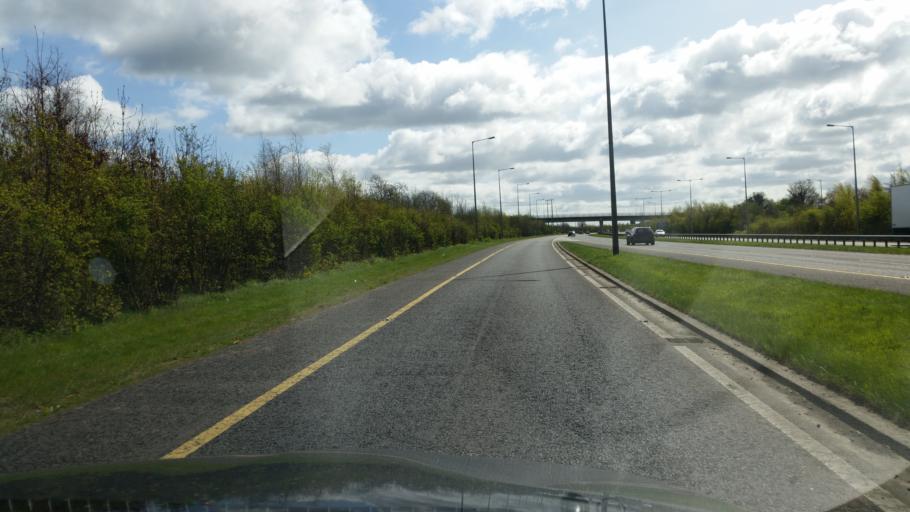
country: IE
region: Leinster
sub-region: An Mhi
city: Ashbourne
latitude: 53.4875
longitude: -6.3840
